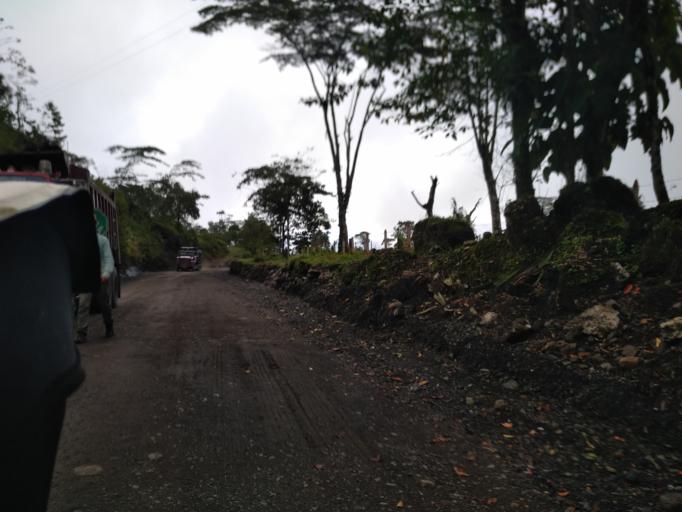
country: CO
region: Santander
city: Landazuri
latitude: 6.1840
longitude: -73.7186
